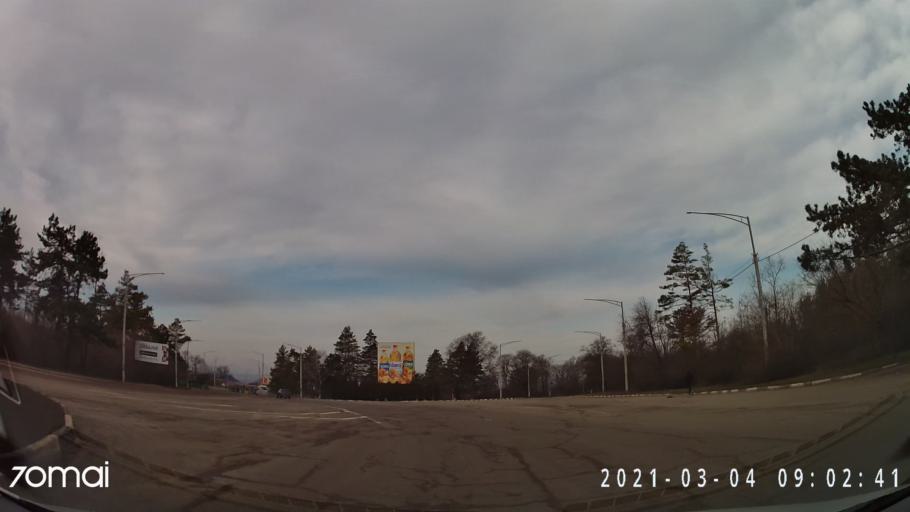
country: MD
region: Balti
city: Balti
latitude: 47.7450
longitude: 27.9527
